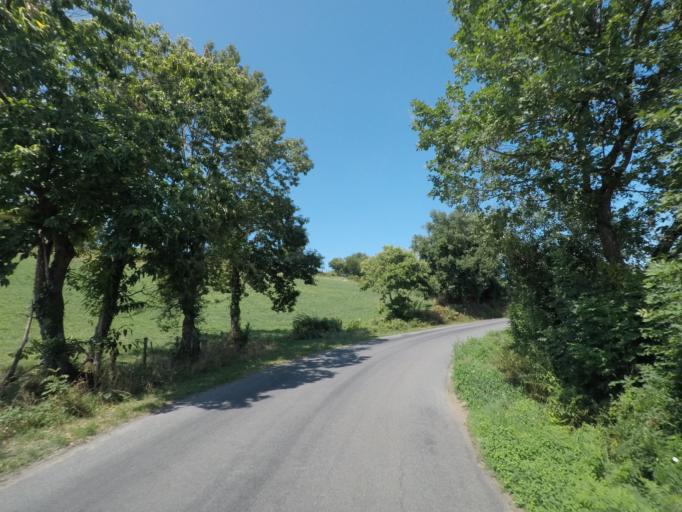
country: FR
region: Midi-Pyrenees
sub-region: Departement de l'Aveyron
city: Livinhac-le-Haut
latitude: 44.6152
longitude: 2.2115
